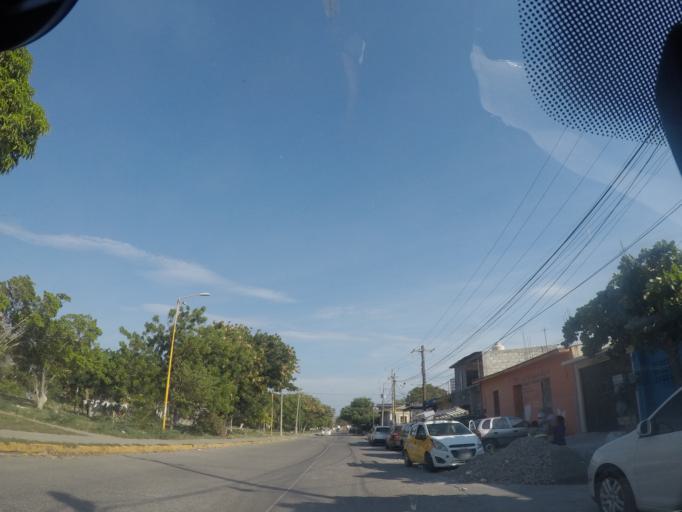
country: MX
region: Oaxaca
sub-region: Salina Cruz
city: Salina Cruz
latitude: 16.1804
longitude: -95.1990
